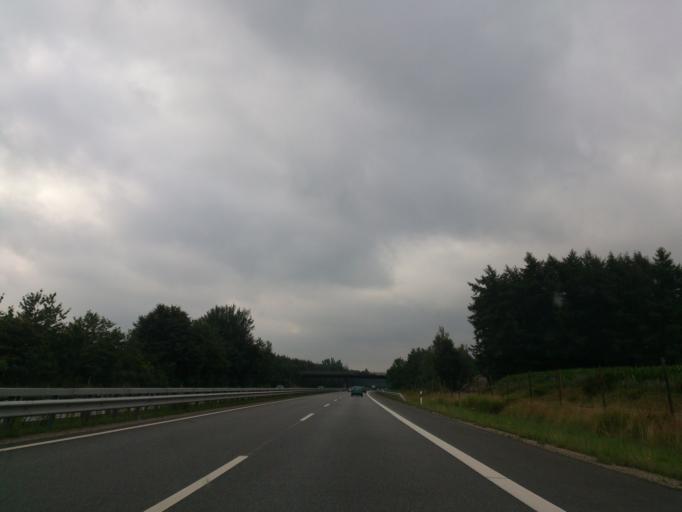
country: DE
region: Schleswig-Holstein
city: Kaaks
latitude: 53.9894
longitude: 9.4892
